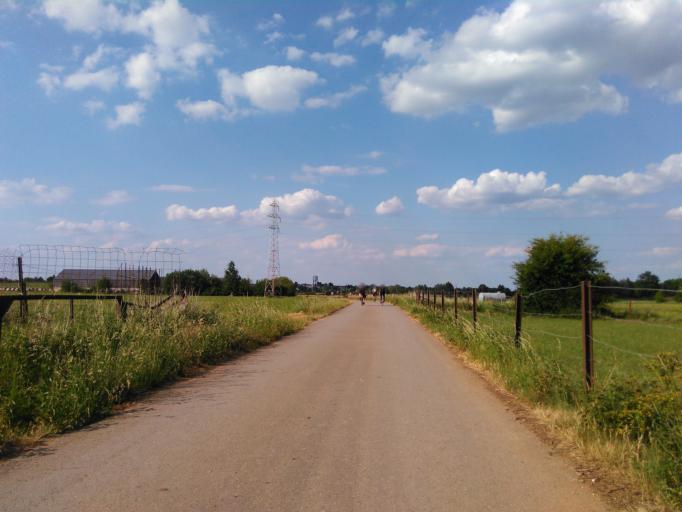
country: LU
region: Luxembourg
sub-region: Canton d'Esch-sur-Alzette
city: Kayl
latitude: 49.4959
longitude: 6.0453
